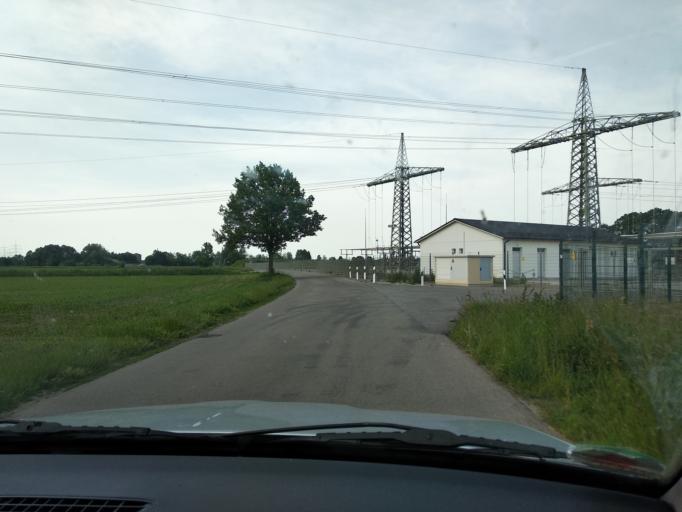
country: DE
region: Bavaria
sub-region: Swabia
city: Woringen
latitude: 47.9385
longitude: 10.2125
